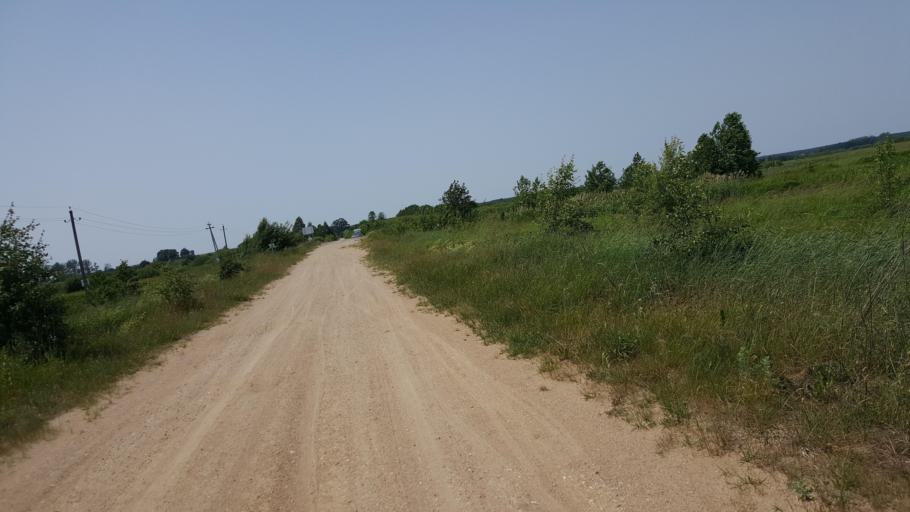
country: BY
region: Brest
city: Kamyanyets
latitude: 52.4757
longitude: 23.9009
